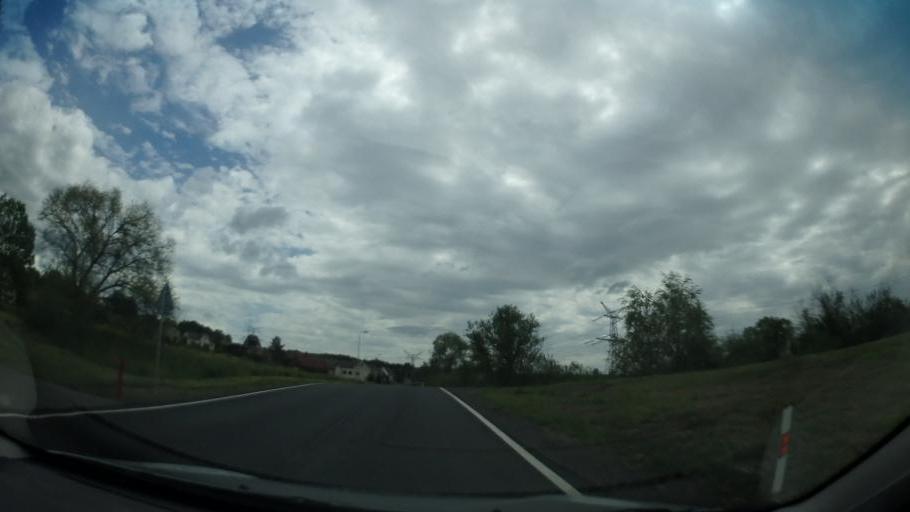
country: CZ
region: Pardubicky
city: Kuncina
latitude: 49.8494
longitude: 16.6949
